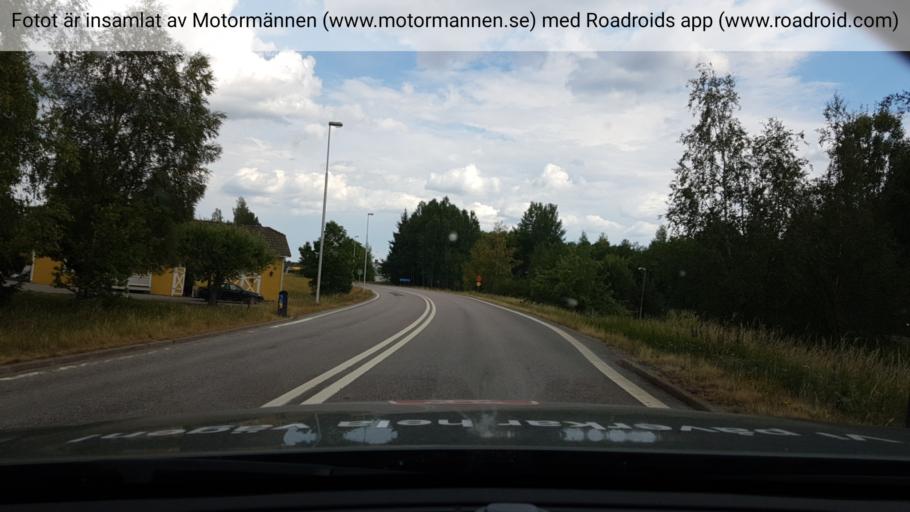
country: SE
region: Uppsala
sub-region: Heby Kommun
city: Morgongava
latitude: 59.9039
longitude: 17.0573
